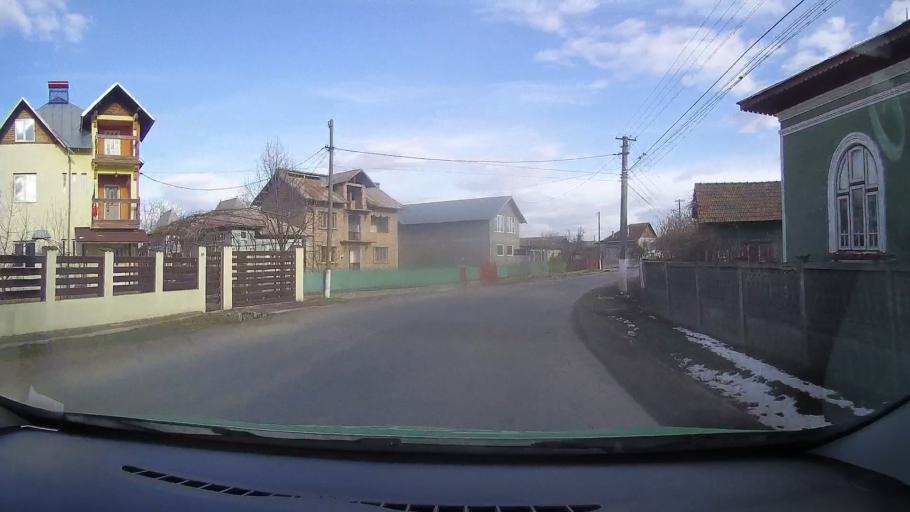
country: RO
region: Dambovita
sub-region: Comuna Vacaresti
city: Bungetu
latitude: 44.8668
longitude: 25.5215
